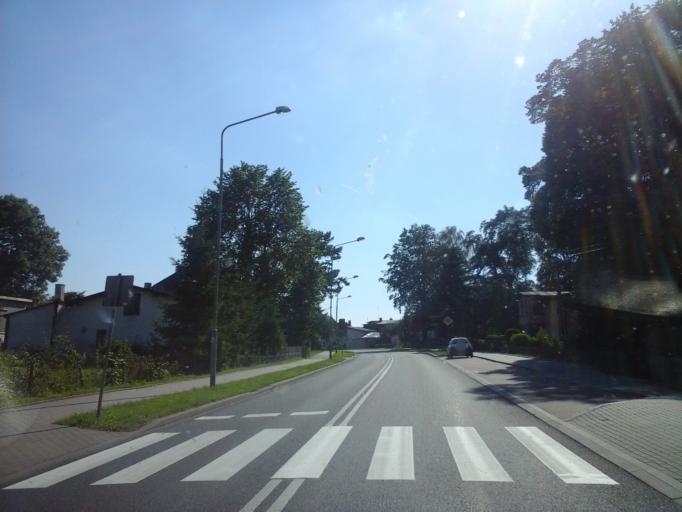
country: PL
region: West Pomeranian Voivodeship
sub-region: Powiat kolobrzeski
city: Ryman
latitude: 53.9470
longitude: 15.5340
